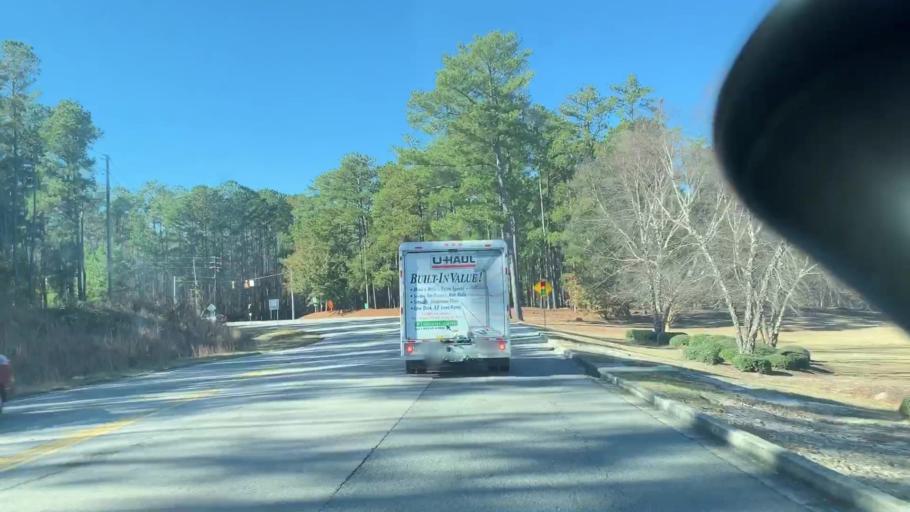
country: US
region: South Carolina
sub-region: Richland County
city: Woodfield
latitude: 34.0721
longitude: -80.9141
